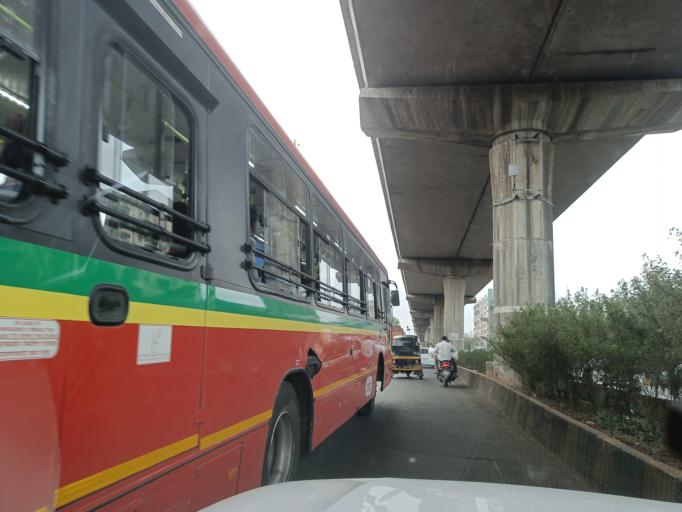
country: IN
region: Maharashtra
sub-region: Mumbai Suburban
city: Powai
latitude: 19.0954
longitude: 72.8964
